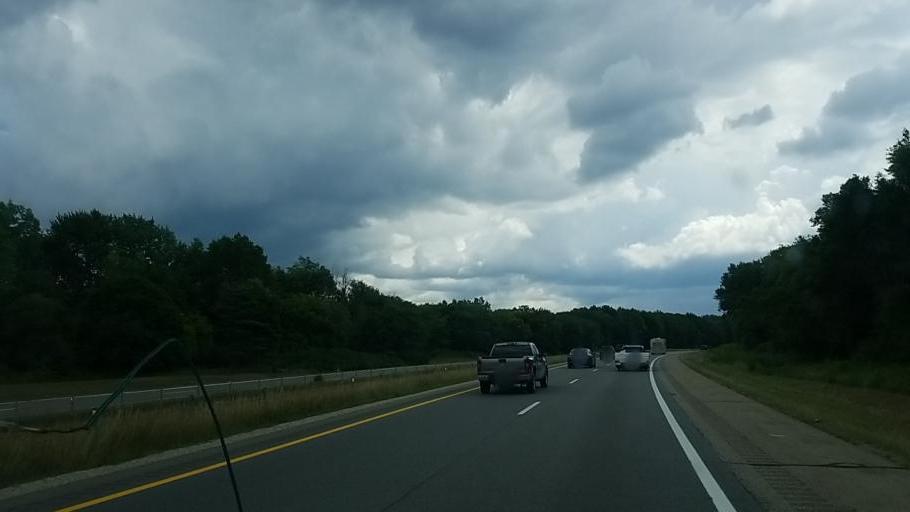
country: US
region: Michigan
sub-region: Kent County
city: Northview
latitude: 43.0109
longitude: -85.6079
